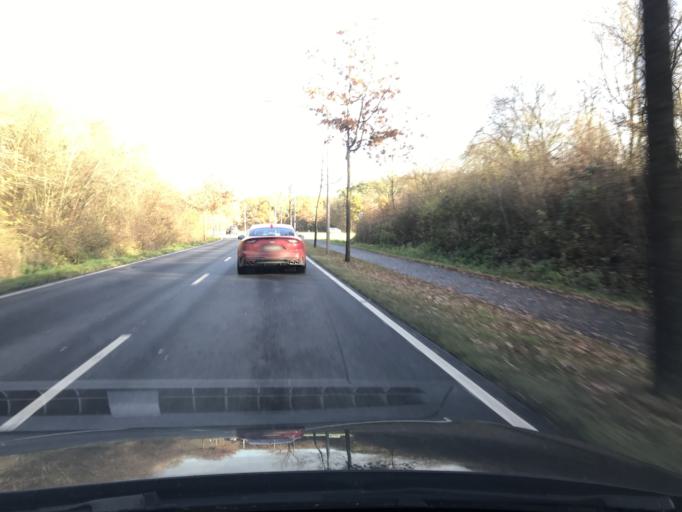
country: DE
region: North Rhine-Westphalia
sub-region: Regierungsbezirk Arnsberg
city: Hamm
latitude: 51.6624
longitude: 7.8541
